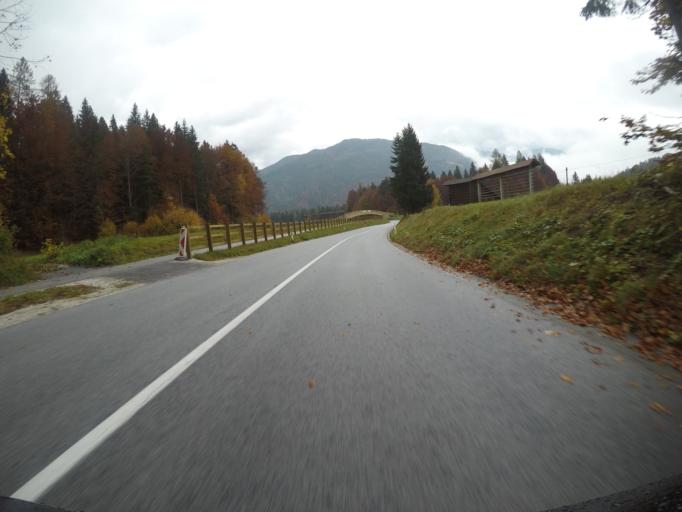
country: SI
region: Kranjska Gora
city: Kranjska Gora
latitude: 46.4850
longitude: 13.7236
